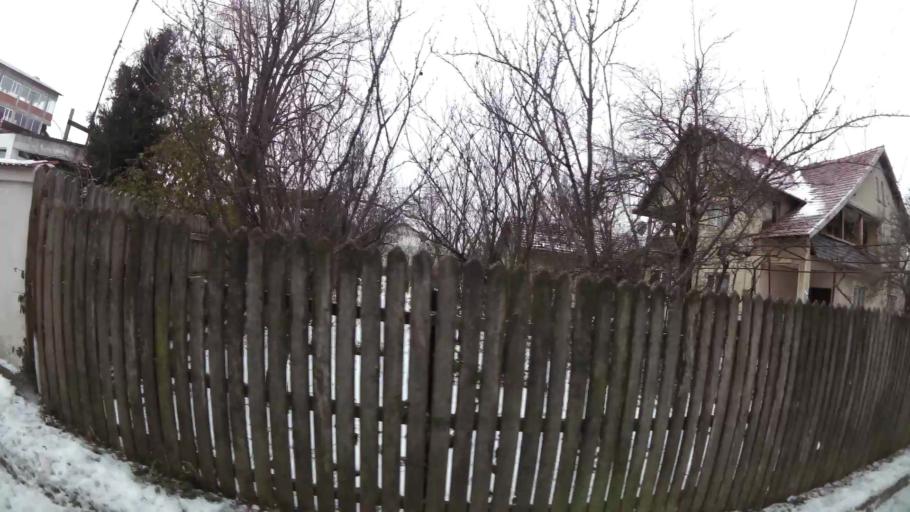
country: RO
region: Dambovita
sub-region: Municipiul Targoviste
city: Targoviste
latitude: 44.9358
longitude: 25.4741
